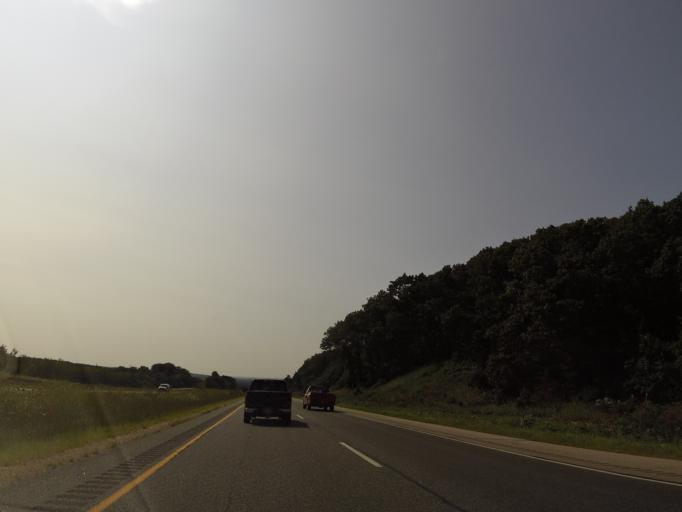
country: US
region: Wisconsin
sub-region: Monroe County
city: Tomah
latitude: 43.9393
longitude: -90.6071
